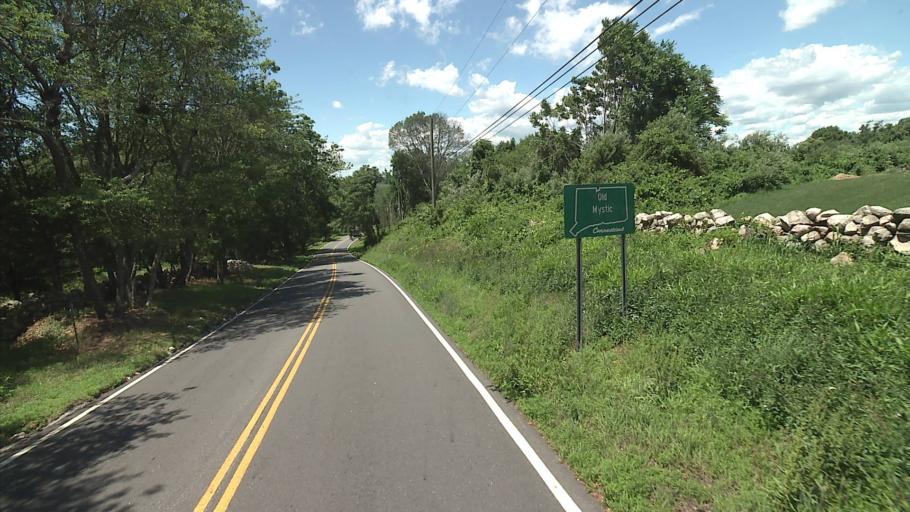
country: US
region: Connecticut
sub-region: New London County
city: Old Mystic
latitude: 41.3870
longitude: -71.9512
